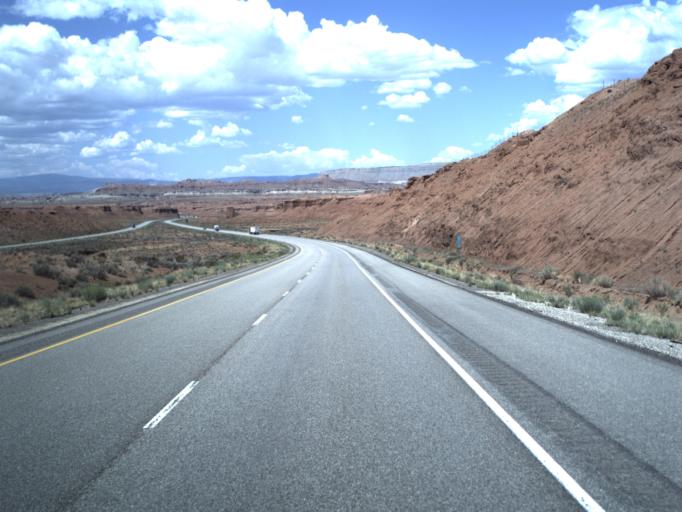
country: US
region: Utah
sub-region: Emery County
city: Ferron
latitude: 38.8476
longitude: -111.0275
